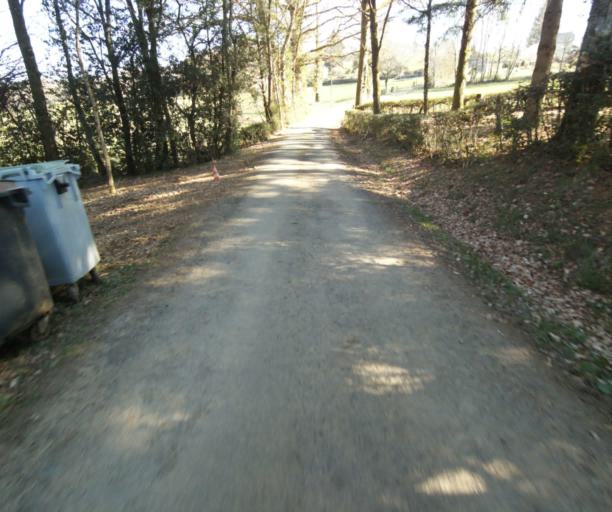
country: FR
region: Limousin
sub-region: Departement de la Correze
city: Seilhac
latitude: 45.3951
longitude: 1.7612
